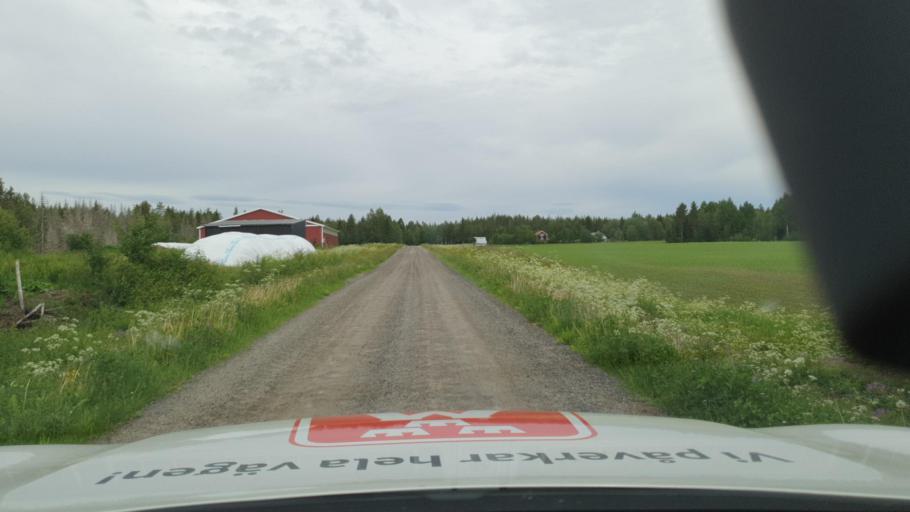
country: SE
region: Vaesterbotten
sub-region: Robertsfors Kommun
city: Robertsfors
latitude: 64.1876
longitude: 20.7276
